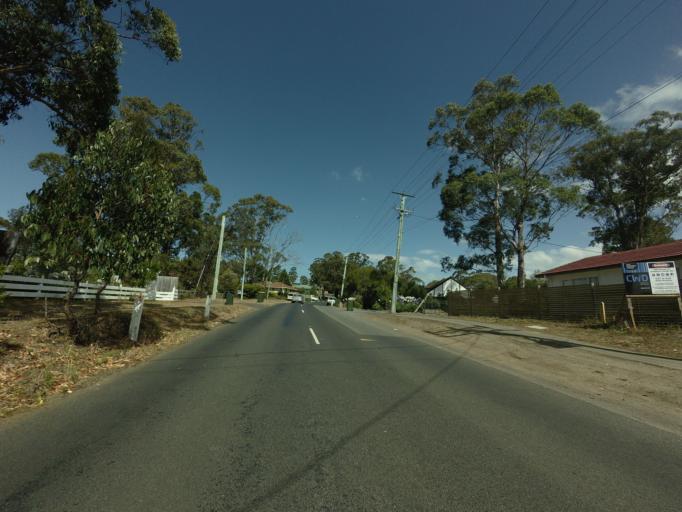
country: AU
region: Tasmania
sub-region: Hobart
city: Dynnyrne
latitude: -42.9216
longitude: 147.3236
